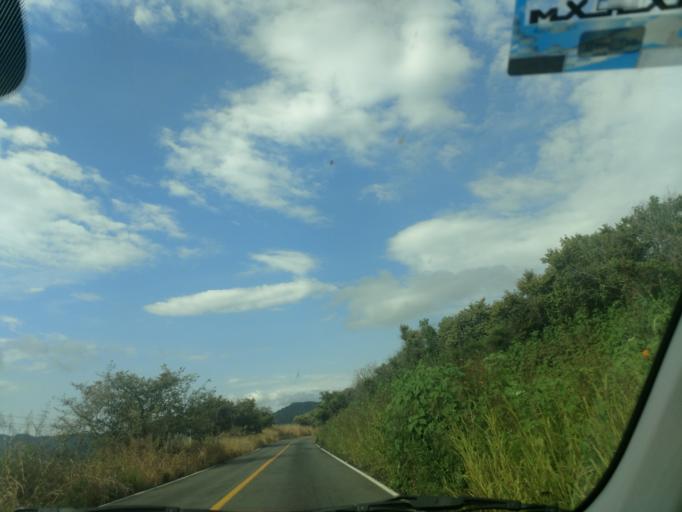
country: MX
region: Jalisco
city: Ameca
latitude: 20.5313
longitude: -104.2048
